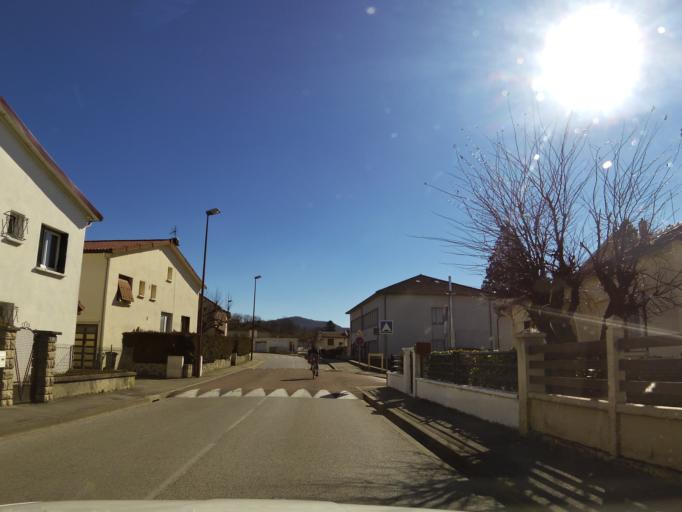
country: FR
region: Rhone-Alpes
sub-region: Departement de l'Ain
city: Amberieu-en-Bugey
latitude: 45.9603
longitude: 5.3601
